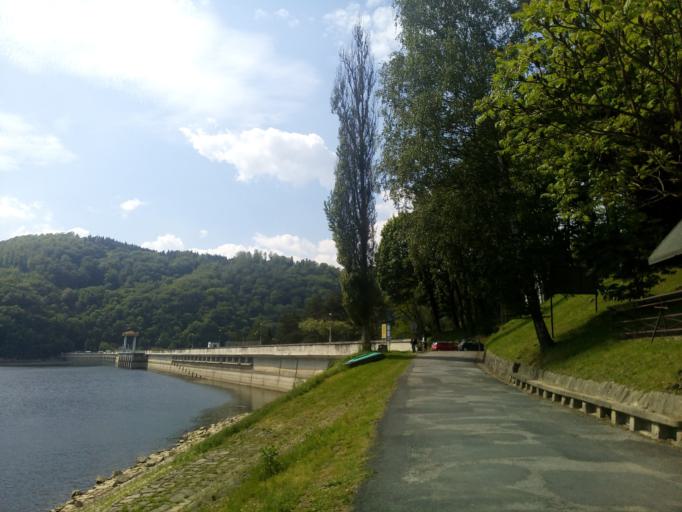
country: PL
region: Lesser Poland Voivodeship
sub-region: Powiat nowosadecki
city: Lososina Dolna
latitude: 49.7606
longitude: 20.6674
